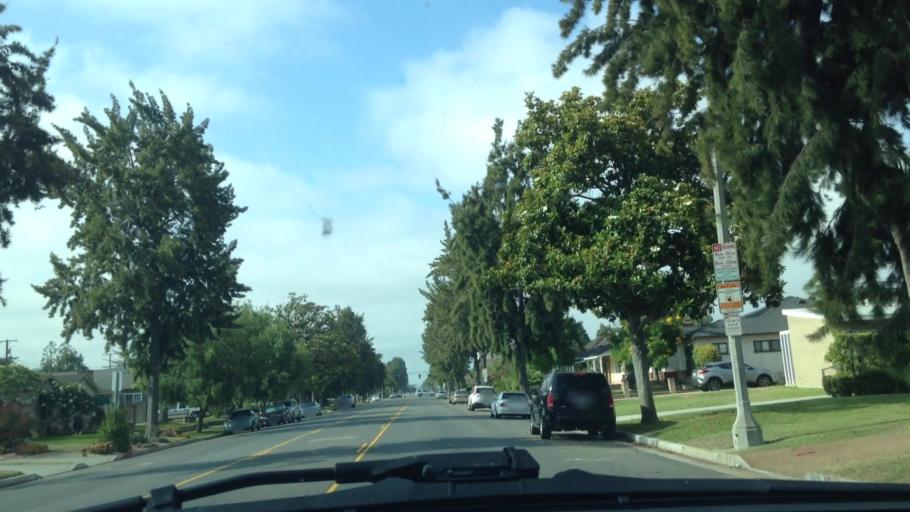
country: US
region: California
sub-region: Los Angeles County
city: Lakewood
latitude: 33.8390
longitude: -118.1339
